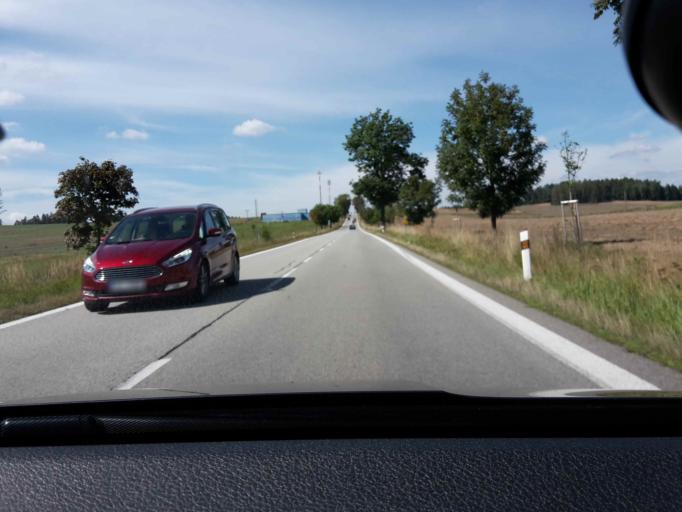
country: CZ
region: Jihocesky
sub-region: Okres Jindrichuv Hradec
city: Jindrichuv Hradec
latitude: 49.1609
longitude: 14.9478
